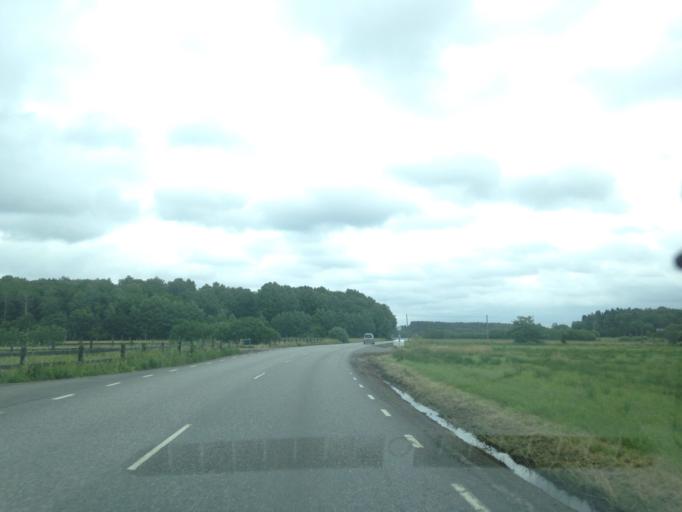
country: SE
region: Vaestra Goetaland
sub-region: Kungalvs Kommun
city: Kode
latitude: 57.8569
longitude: 11.8638
